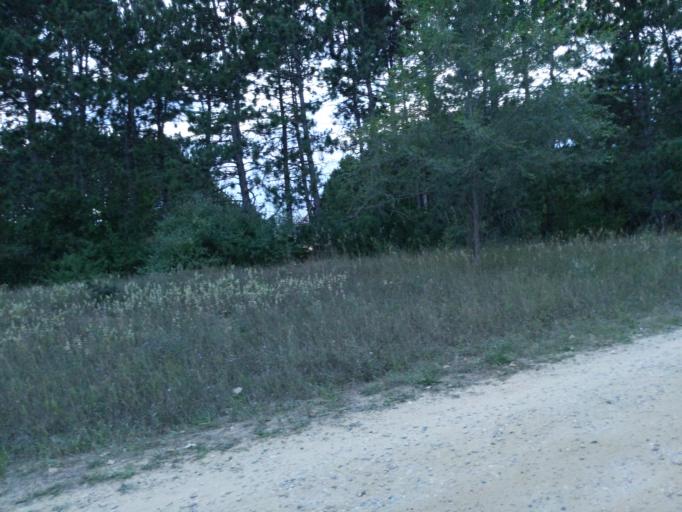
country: US
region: Michigan
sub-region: Isabella County
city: Mount Pleasant
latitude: 43.5811
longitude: -84.8474
